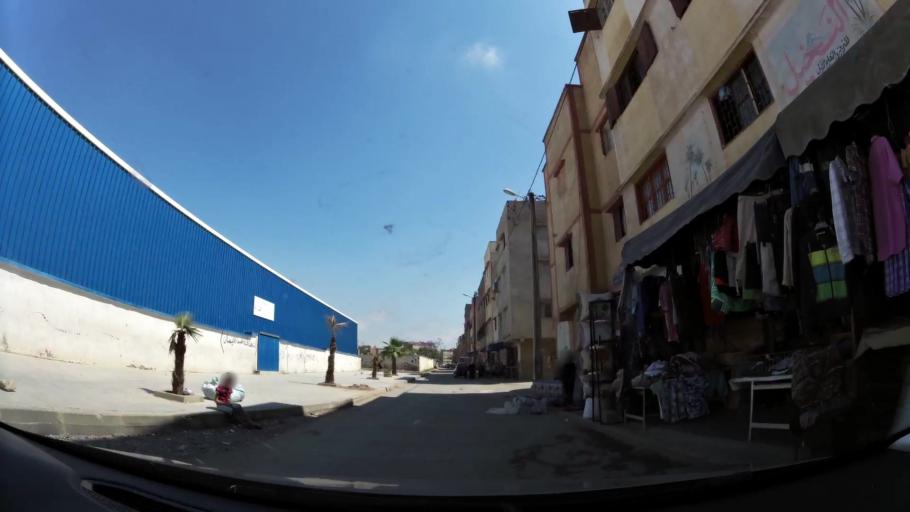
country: MA
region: Rabat-Sale-Zemmour-Zaer
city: Sale
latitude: 34.0621
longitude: -6.7785
